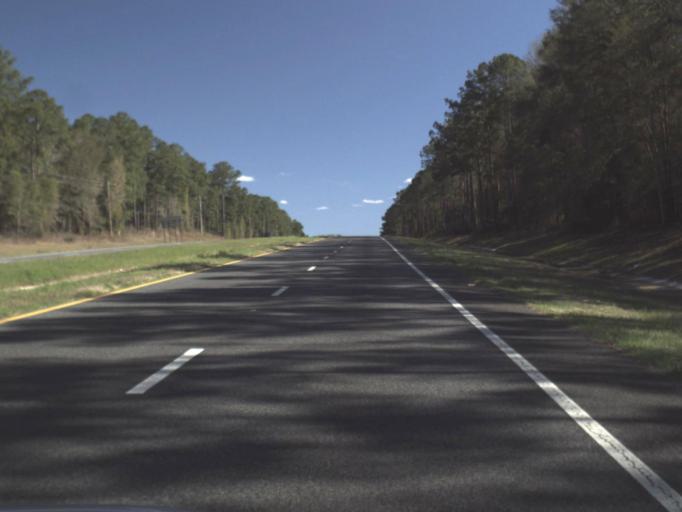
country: US
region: Florida
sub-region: Gadsden County
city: Midway
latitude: 30.5444
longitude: -84.4832
